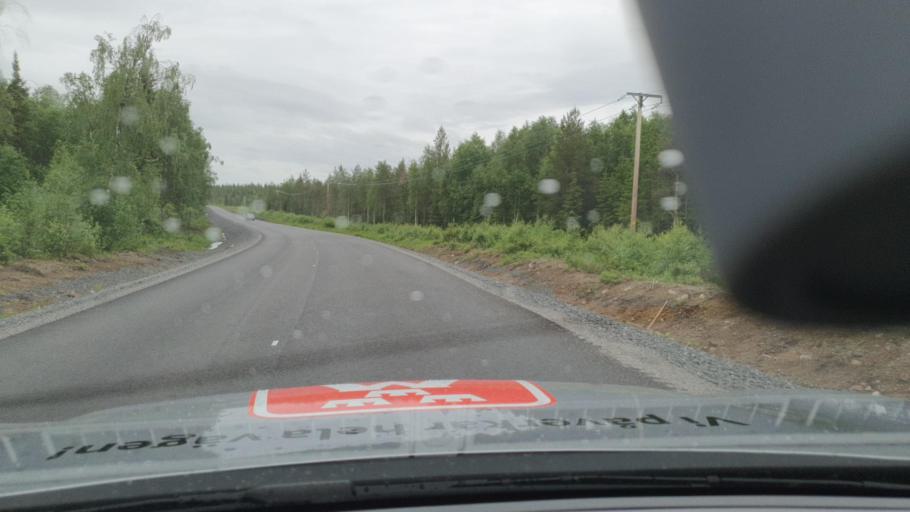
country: SE
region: Norrbotten
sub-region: Overkalix Kommun
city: OEverkalix
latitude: 66.7033
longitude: 23.2049
